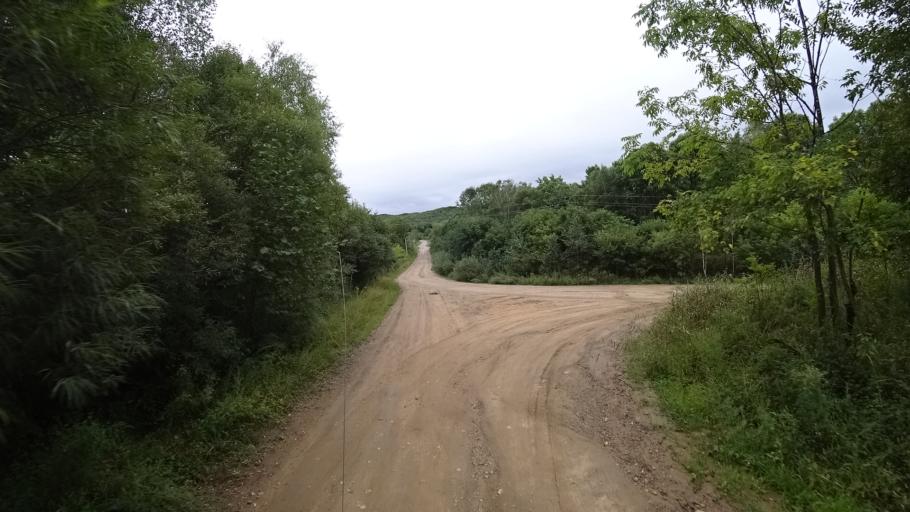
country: RU
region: Primorskiy
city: Rettikhovka
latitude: 44.1698
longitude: 132.7838
